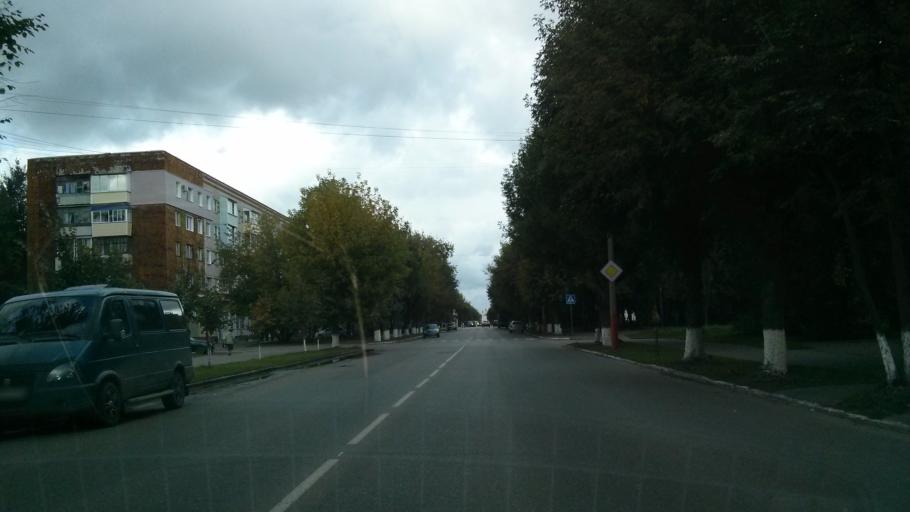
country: RU
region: Vladimir
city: Murom
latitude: 55.5701
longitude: 42.0542
